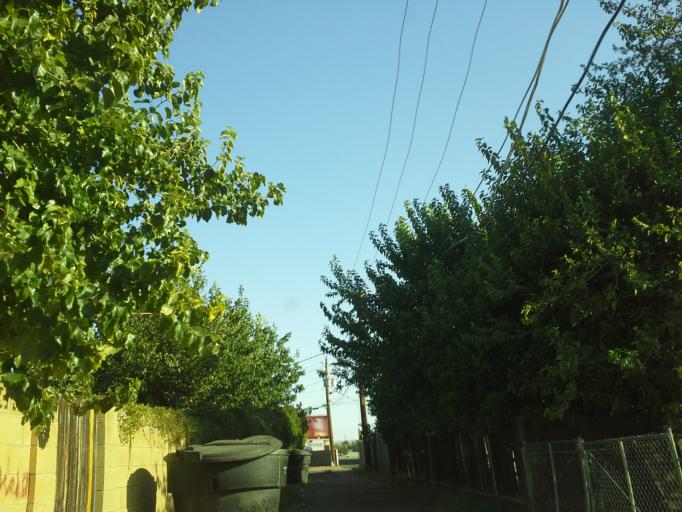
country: US
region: Arizona
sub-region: Maricopa County
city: Phoenix
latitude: 33.5260
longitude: -112.0991
